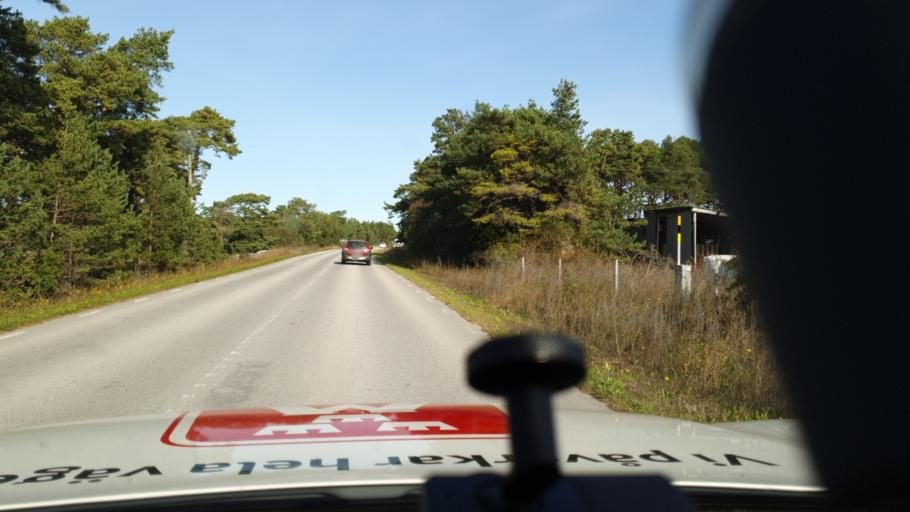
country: SE
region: Gotland
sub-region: Gotland
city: Slite
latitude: 57.8787
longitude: 19.0869
